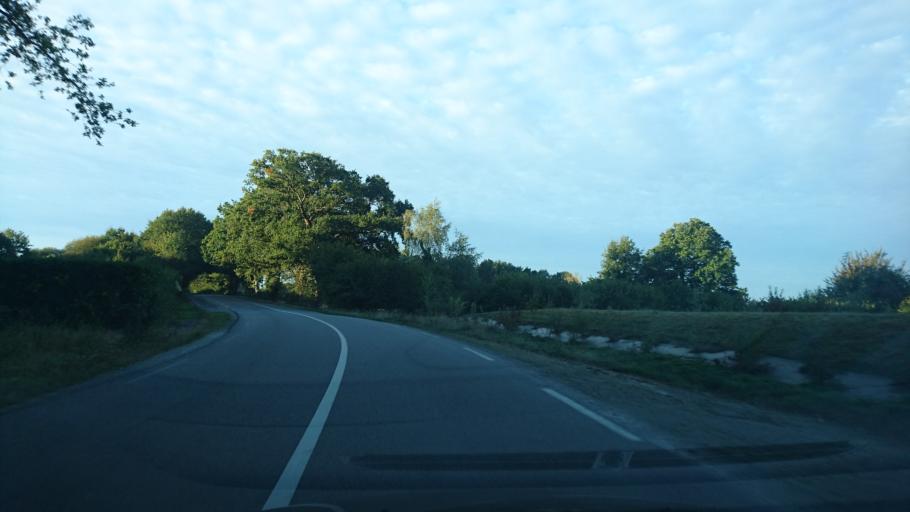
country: FR
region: Brittany
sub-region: Departement d'Ille-et-Vilaine
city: Bains-sur-Oust
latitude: 47.6883
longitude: -2.0579
